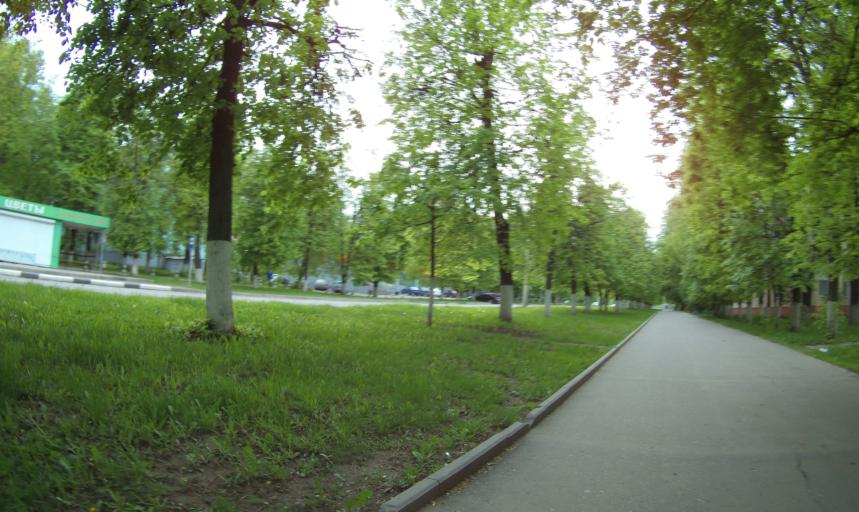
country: RU
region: Moskovskaya
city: Kolomna
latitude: 55.0866
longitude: 38.7707
